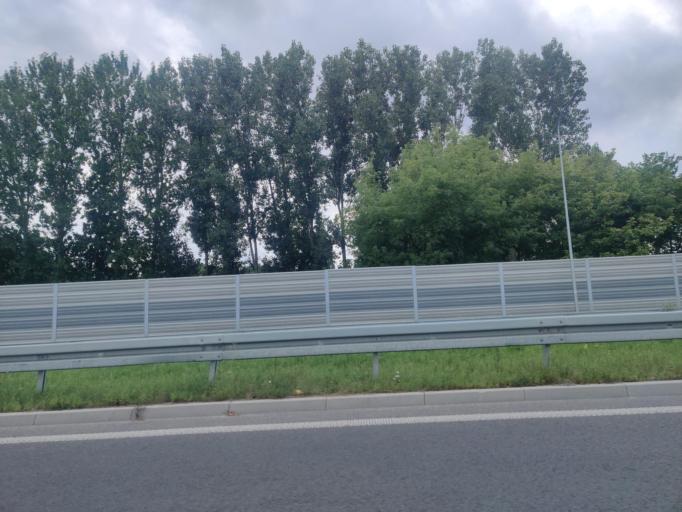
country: PL
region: Greater Poland Voivodeship
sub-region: Konin
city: Konin
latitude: 52.2046
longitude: 18.2696
